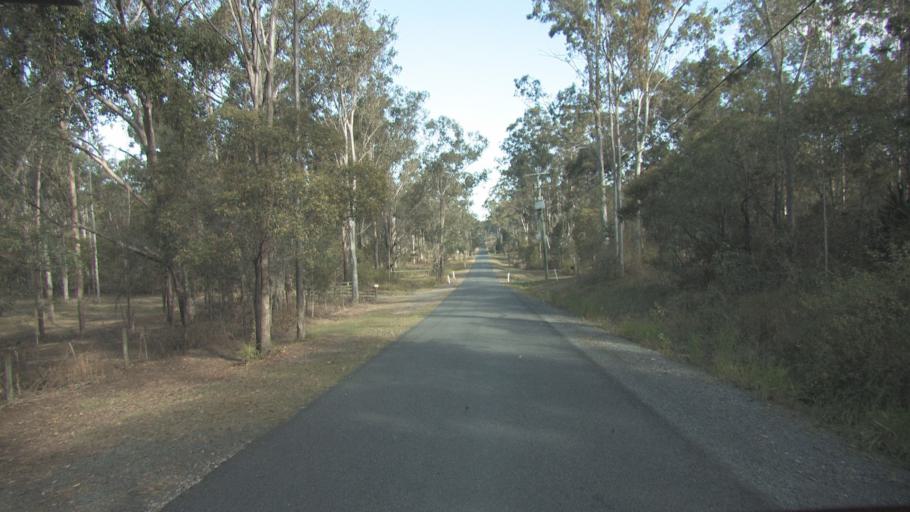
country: AU
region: Queensland
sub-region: Logan
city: North Maclean
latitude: -27.8224
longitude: 153.0632
